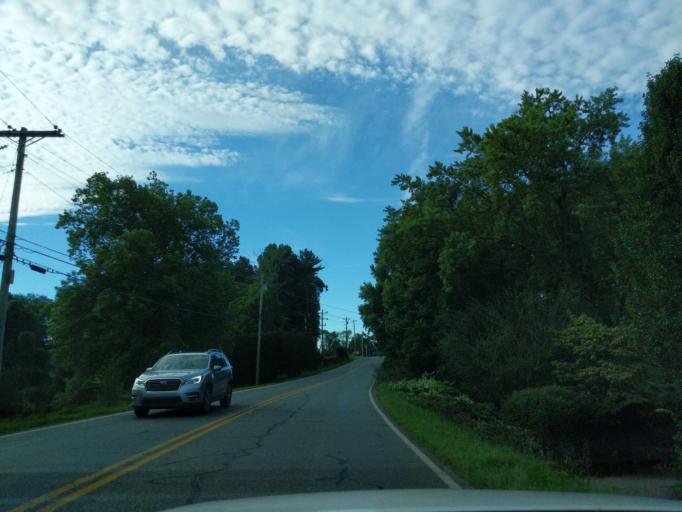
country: US
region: Georgia
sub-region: Fannin County
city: McCaysville
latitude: 34.9713
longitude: -84.3708
